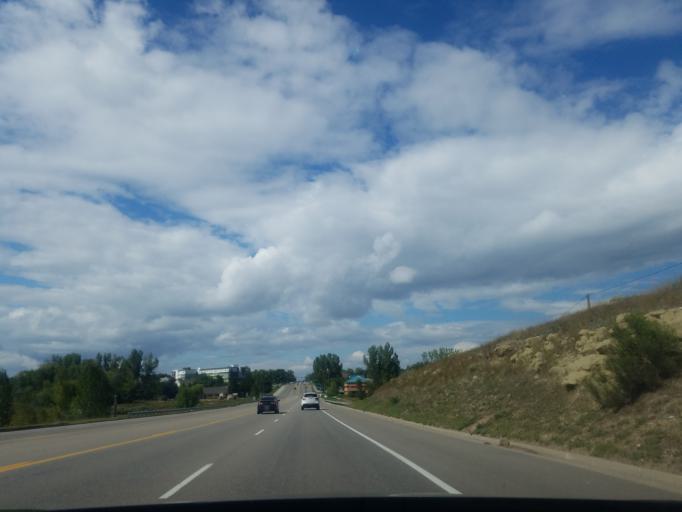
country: US
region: Colorado
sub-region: Larimer County
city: Fort Collins
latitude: 40.5116
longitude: -105.0773
